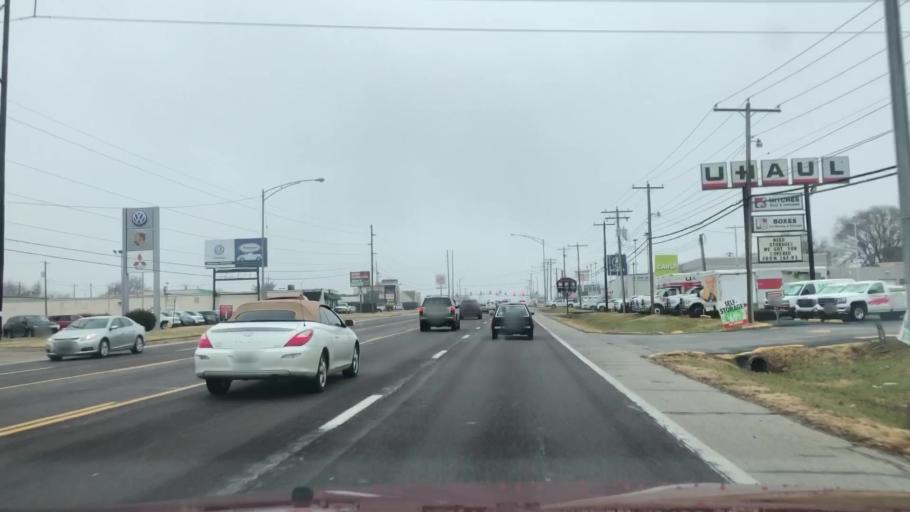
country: US
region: Missouri
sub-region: Greene County
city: Springfield
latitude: 37.1570
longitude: -93.2955
